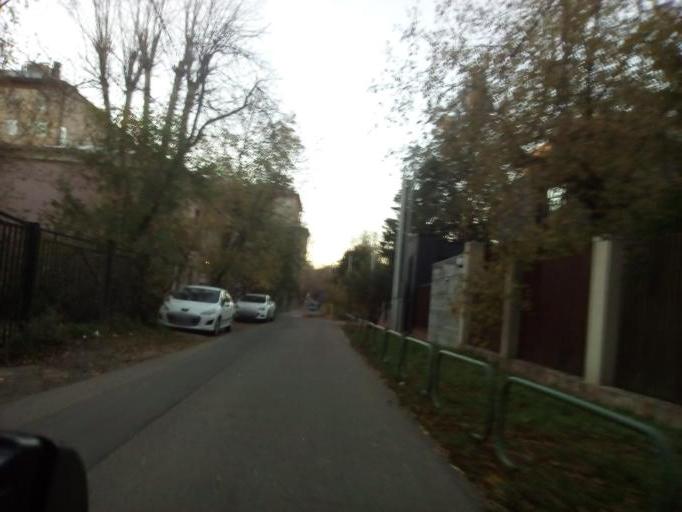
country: RU
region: Moscow
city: Sokol
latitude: 55.8026
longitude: 37.4984
